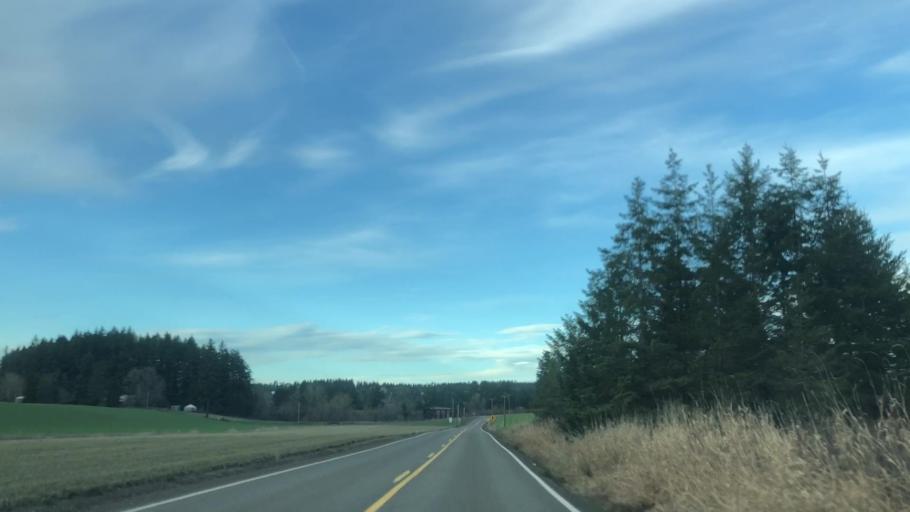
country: US
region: Oregon
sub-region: Washington County
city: Rockcreek
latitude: 45.5896
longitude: -122.9193
